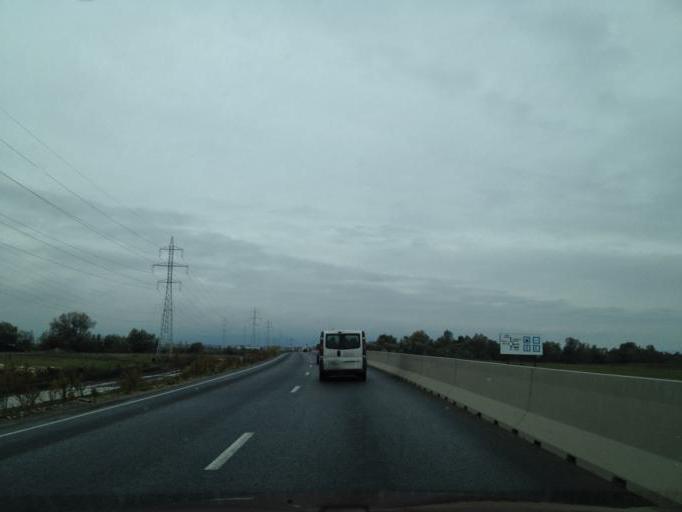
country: RO
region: Brasov
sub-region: Comuna Sanpetru
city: Sanpetru
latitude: 45.6912
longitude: 25.6144
